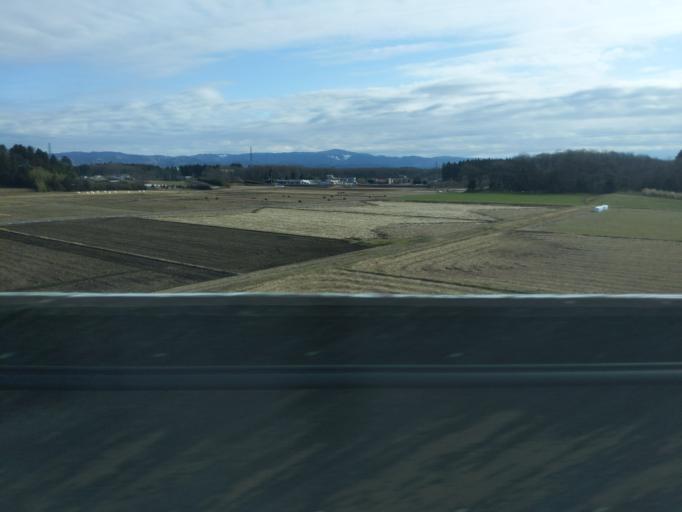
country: JP
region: Tochigi
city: Kuroiso
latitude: 37.0179
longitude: 140.0983
